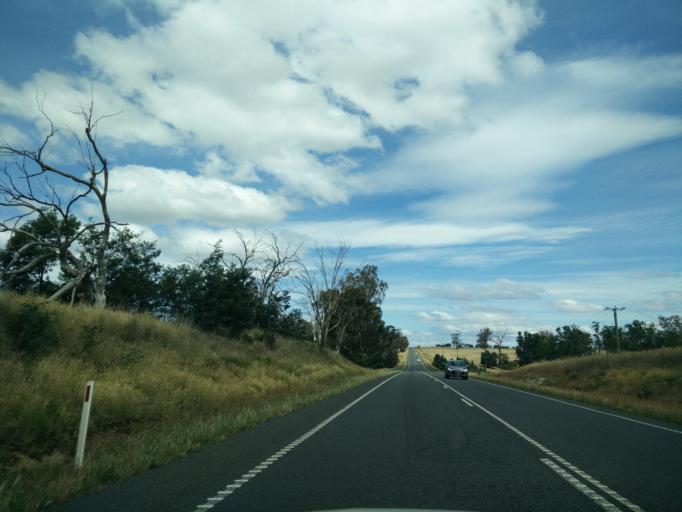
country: AU
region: Tasmania
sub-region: Northern Midlands
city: Evandale
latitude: -41.6989
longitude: 147.2901
